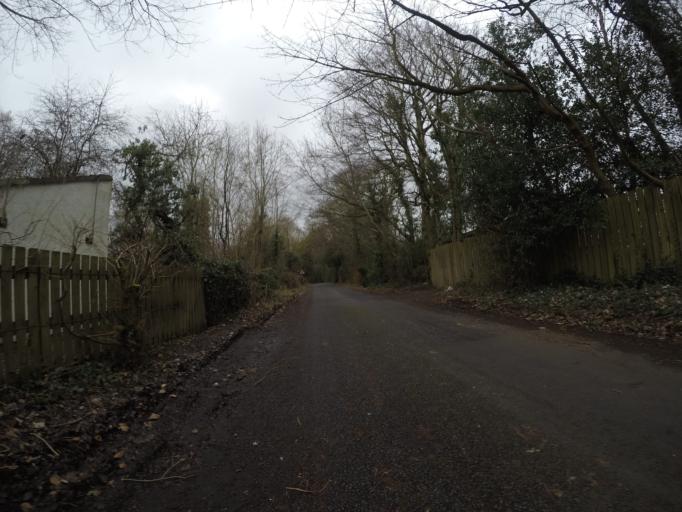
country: GB
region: Scotland
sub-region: North Ayrshire
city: Springside
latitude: 55.6295
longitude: -4.6182
